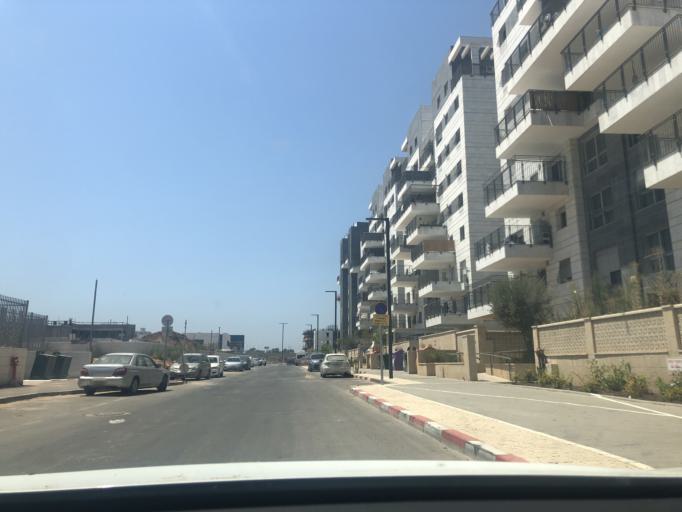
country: IL
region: Central District
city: Lod
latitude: 31.9341
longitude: 34.8983
